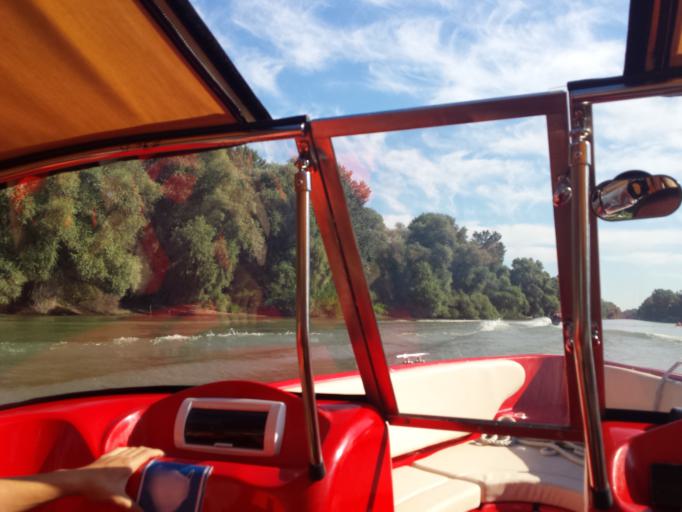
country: RO
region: Tulcea
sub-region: Comuna Nufaru
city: Malcoci
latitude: 45.2127
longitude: 28.8640
